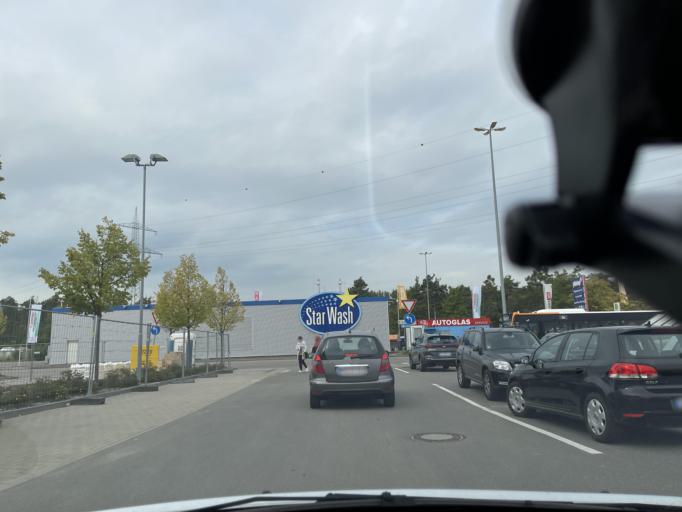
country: DE
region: Hesse
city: Viernheim
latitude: 49.5203
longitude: 8.5556
